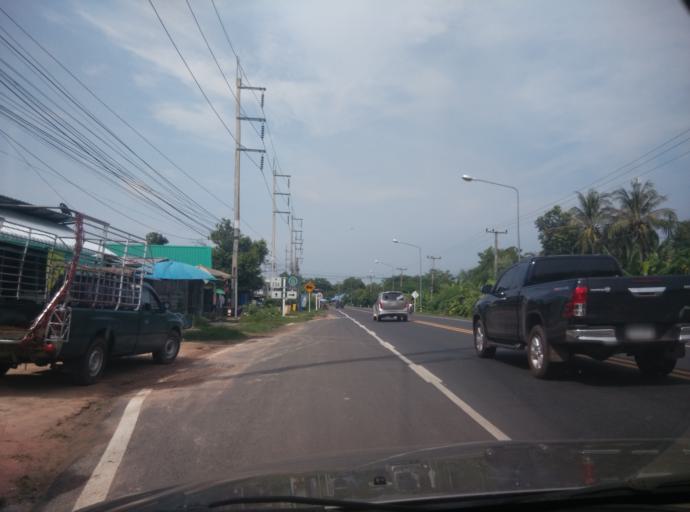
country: TH
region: Sisaket
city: Uthumphon Phisai
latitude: 15.1023
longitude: 104.1262
